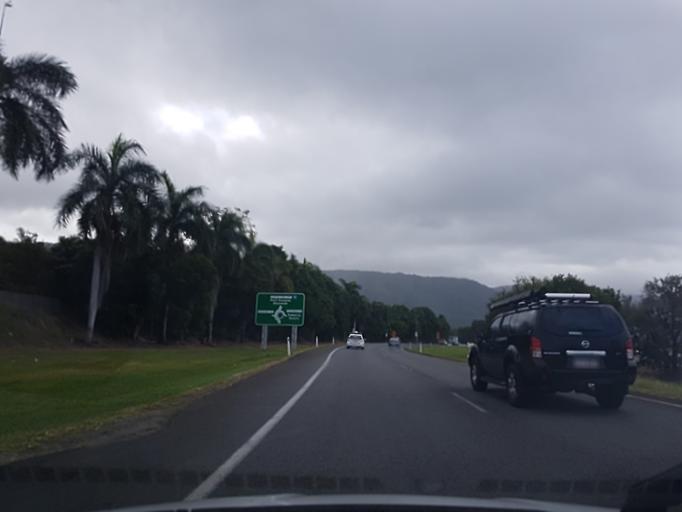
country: AU
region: Queensland
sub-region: Cairns
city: Trinity Beach
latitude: -16.7948
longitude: 145.6805
